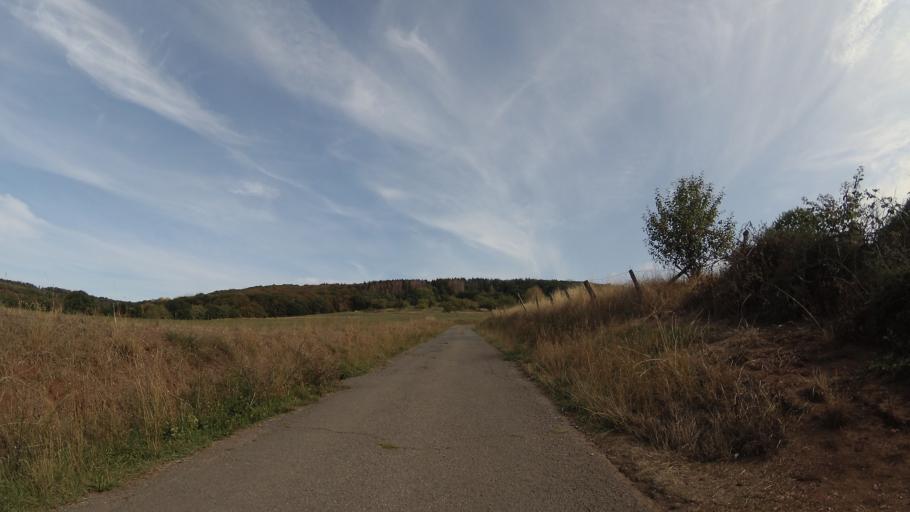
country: DE
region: Saarland
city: Sankt Wendel
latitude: 49.4760
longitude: 7.1830
